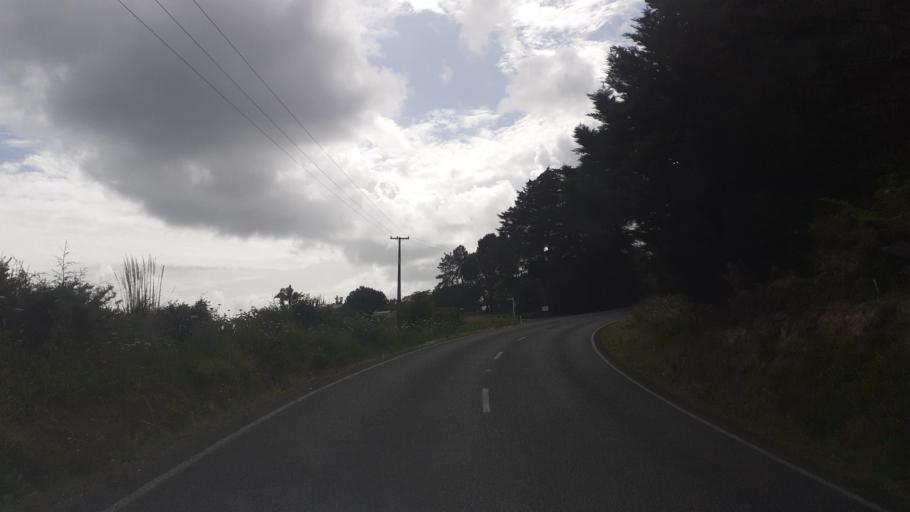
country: NZ
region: Northland
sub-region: Far North District
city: Kerikeri
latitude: -35.2168
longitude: 173.9888
